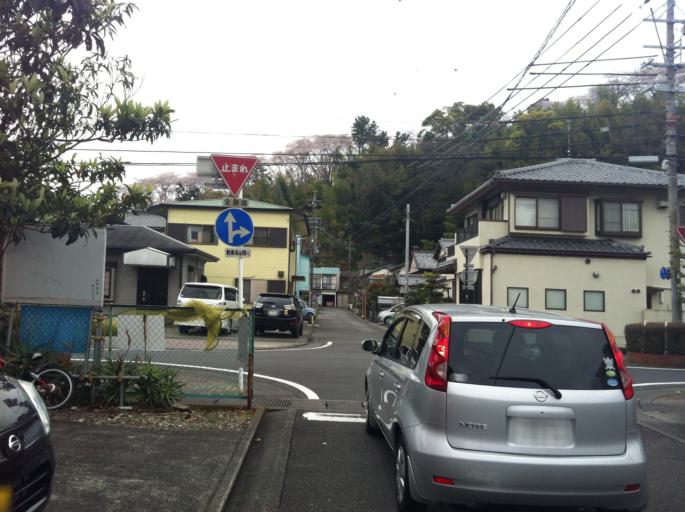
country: JP
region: Shizuoka
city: Shizuoka-shi
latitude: 34.9703
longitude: 138.4047
